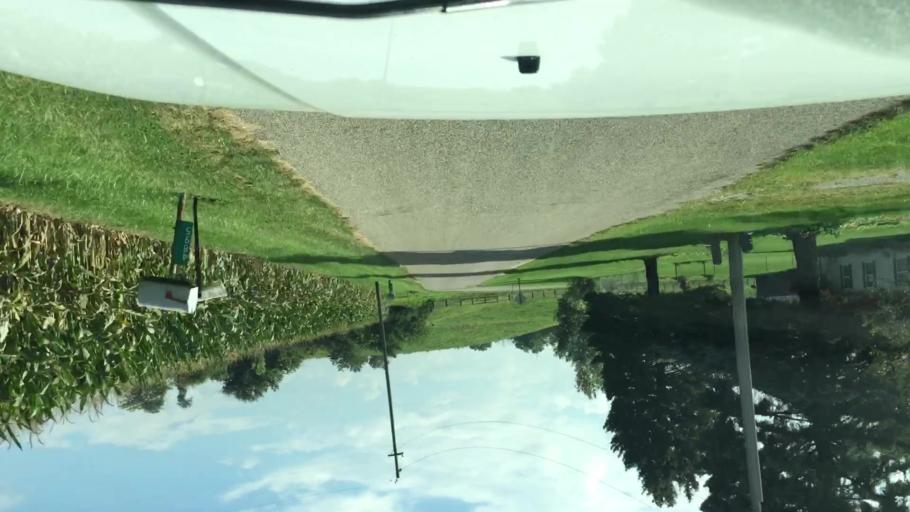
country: US
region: Ohio
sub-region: Champaign County
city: Mechanicsburg
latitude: 40.0608
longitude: -83.6007
